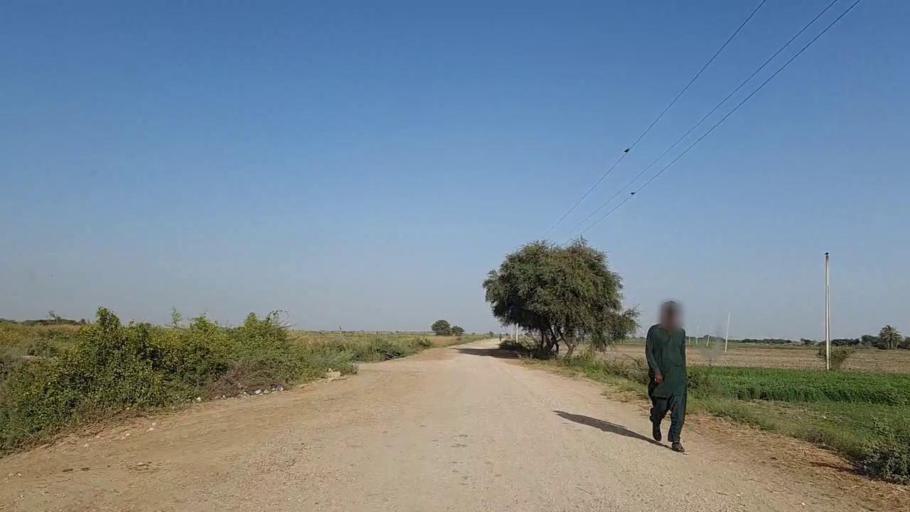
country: PK
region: Sindh
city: Jati
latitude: 24.4233
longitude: 68.2610
